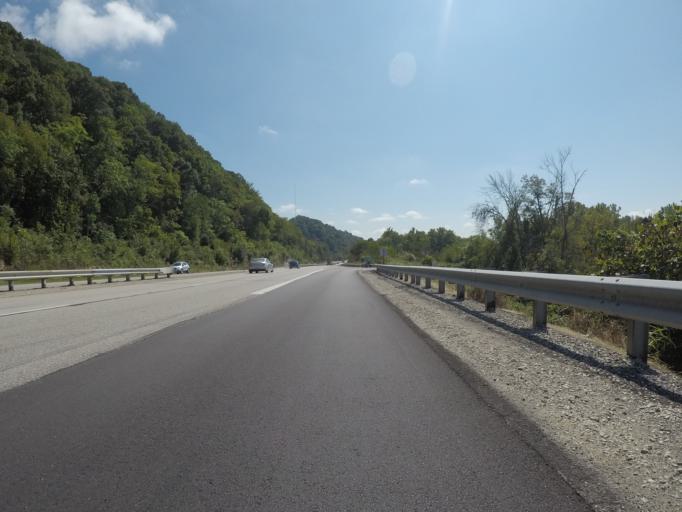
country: US
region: Kentucky
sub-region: Boyd County
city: Ashland
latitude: 38.4722
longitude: -82.6077
